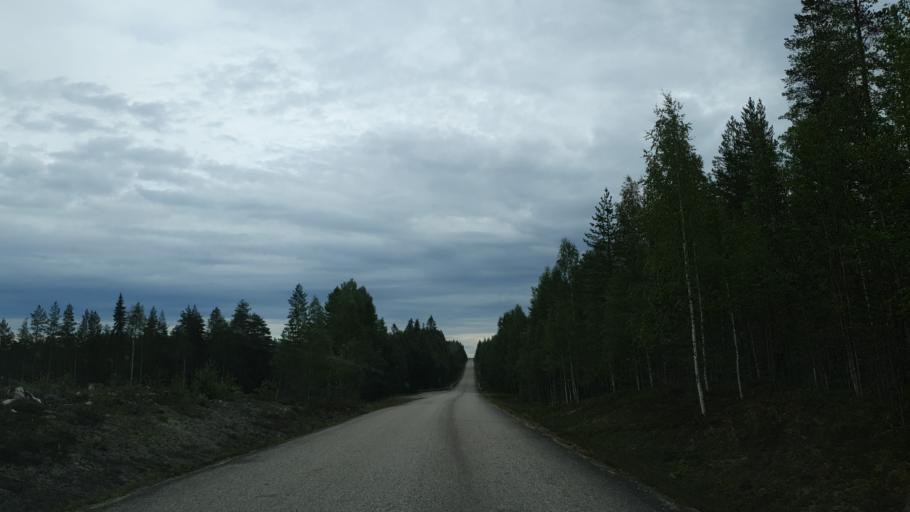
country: FI
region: Kainuu
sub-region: Kehys-Kainuu
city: Kuhmo
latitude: 64.3521
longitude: 29.1041
